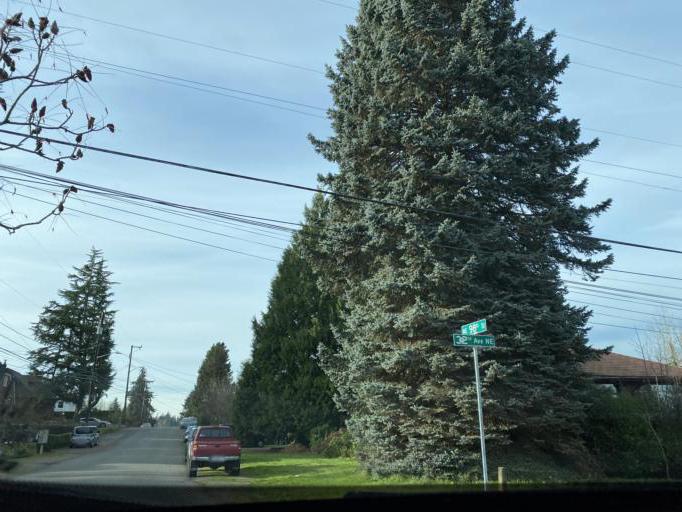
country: US
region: Washington
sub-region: King County
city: Lake Forest Park
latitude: 47.7003
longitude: -122.2933
